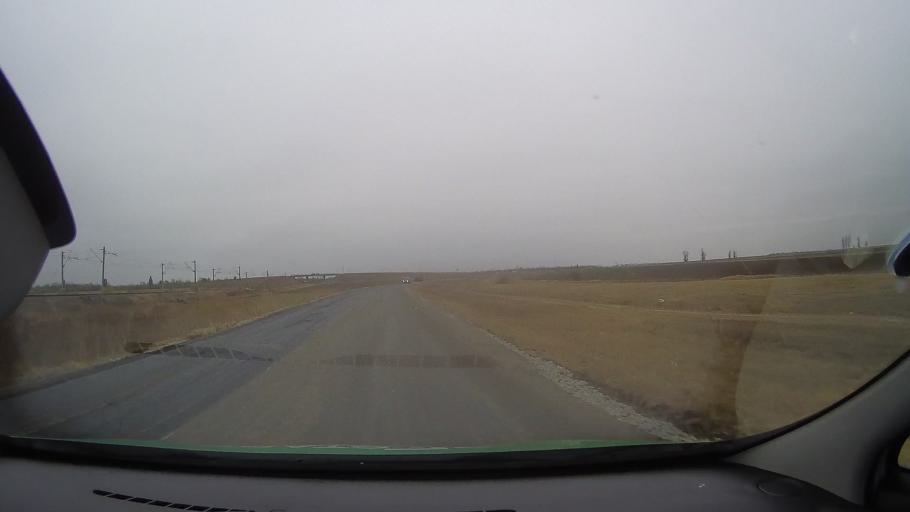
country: RO
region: Braila
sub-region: Comuna Baraganul
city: Baraganul
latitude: 44.8030
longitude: 27.5255
